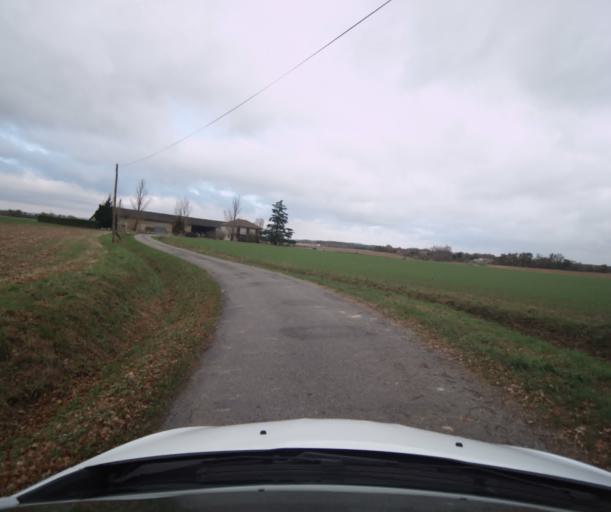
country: FR
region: Midi-Pyrenees
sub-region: Departement du Tarn-et-Garonne
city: Saint-Porquier
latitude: 44.0610
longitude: 1.1718
